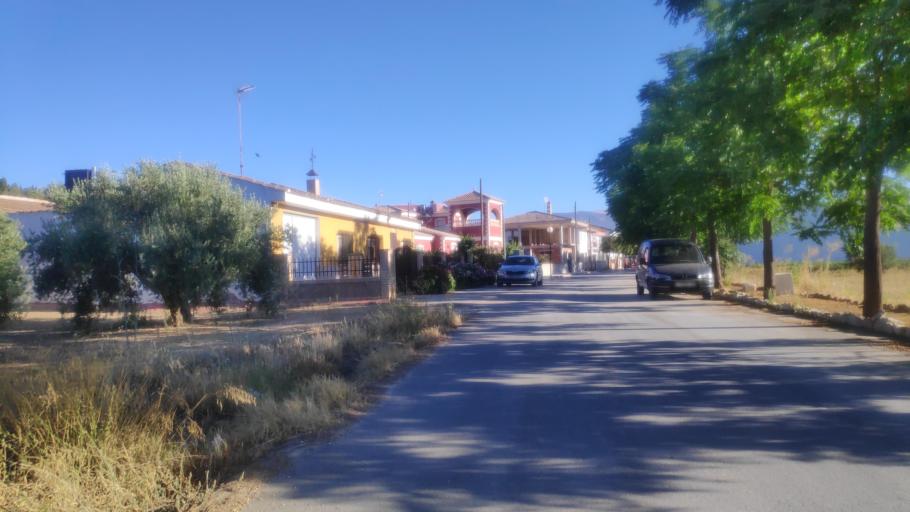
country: ES
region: Andalusia
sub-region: Provincia de Jaen
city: Pozo Alcon
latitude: 37.6703
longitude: -2.9716
